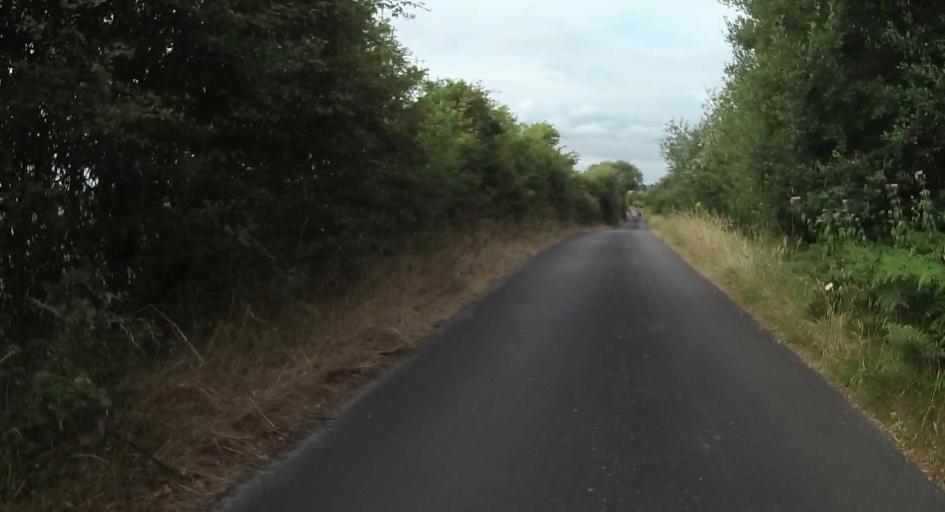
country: GB
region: England
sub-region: Dorset
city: Wareham
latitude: 50.6636
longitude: -2.0859
